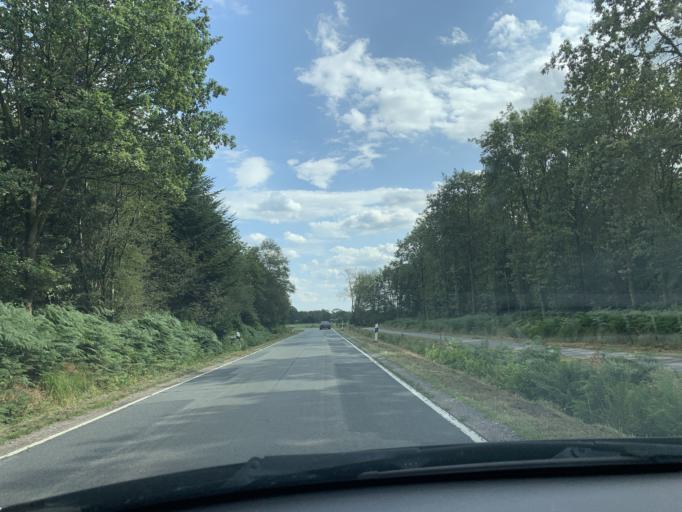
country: DE
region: Lower Saxony
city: Apen
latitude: 53.2555
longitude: 7.8474
